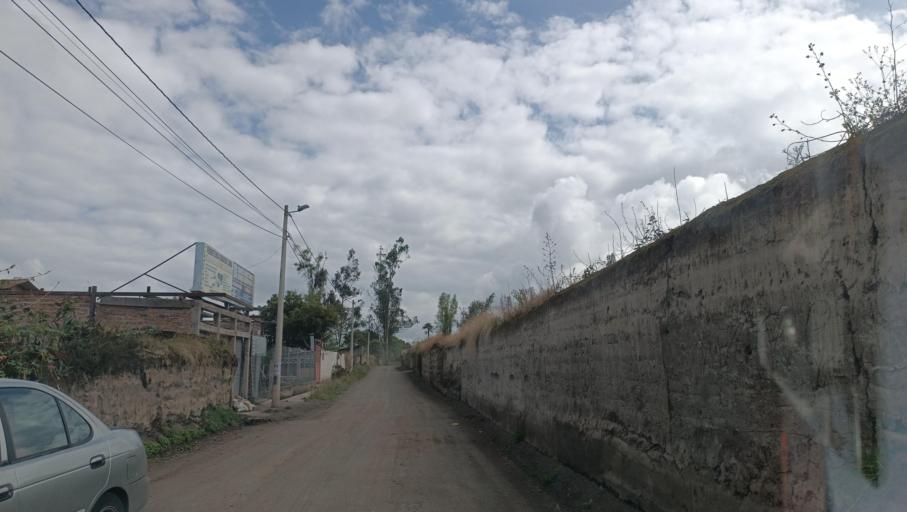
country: EC
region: Chimborazo
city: Guano
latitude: -1.6569
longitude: -78.5679
